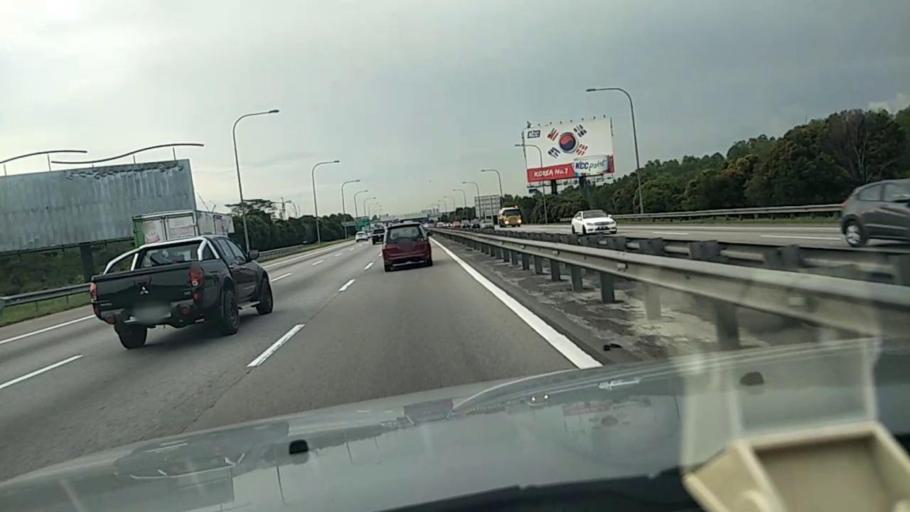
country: MY
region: Putrajaya
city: Putrajaya
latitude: 2.9384
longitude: 101.5959
